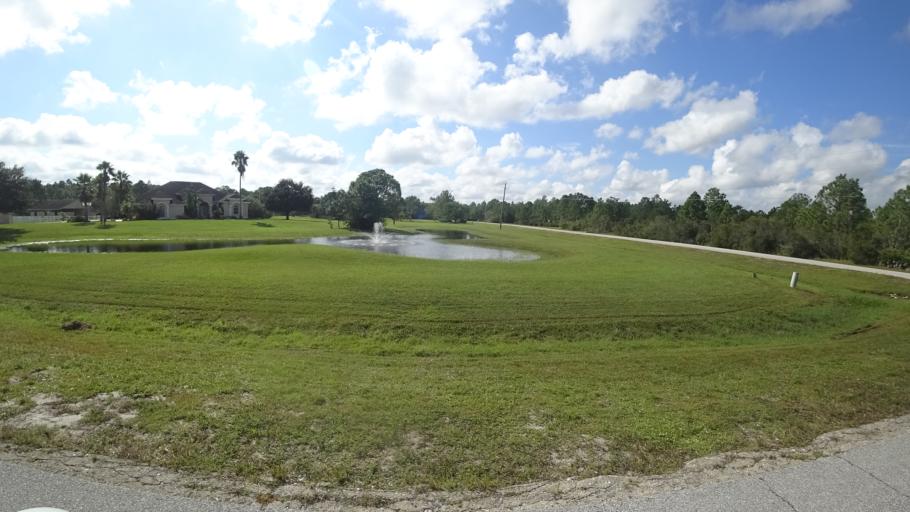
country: US
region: Florida
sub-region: Sarasota County
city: The Meadows
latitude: 27.4024
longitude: -82.3398
